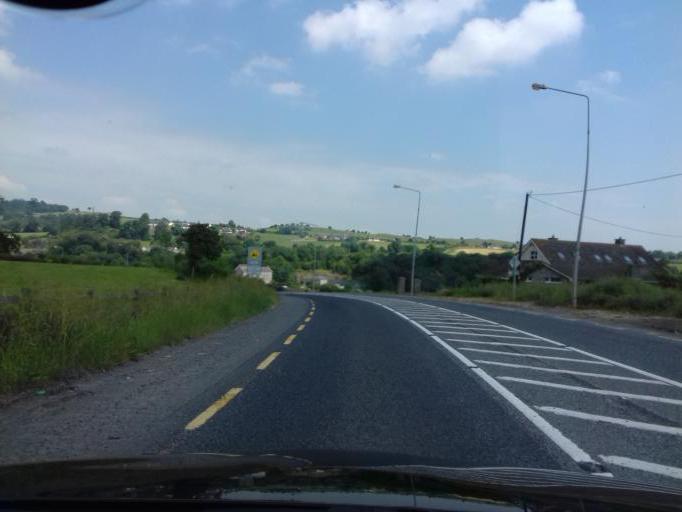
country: IE
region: Leinster
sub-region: An Mhi
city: Slane
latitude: 53.6985
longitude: -6.5379
